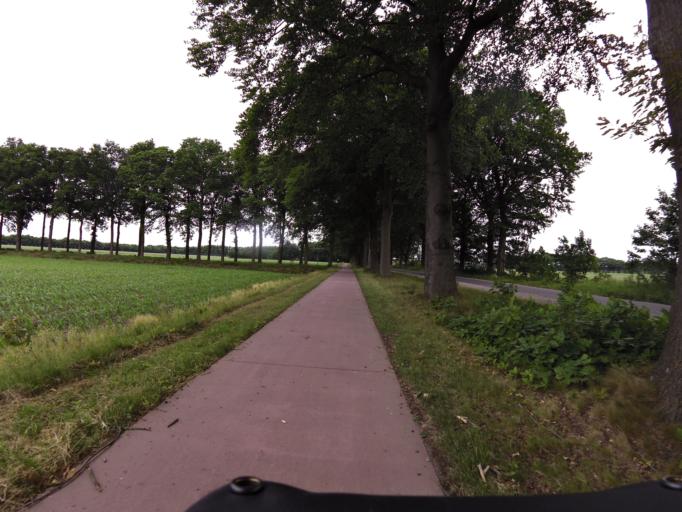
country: NL
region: North Brabant
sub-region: Gemeente Hilvarenbeek
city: Hilvarenbeek
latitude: 51.4250
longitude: 5.0917
